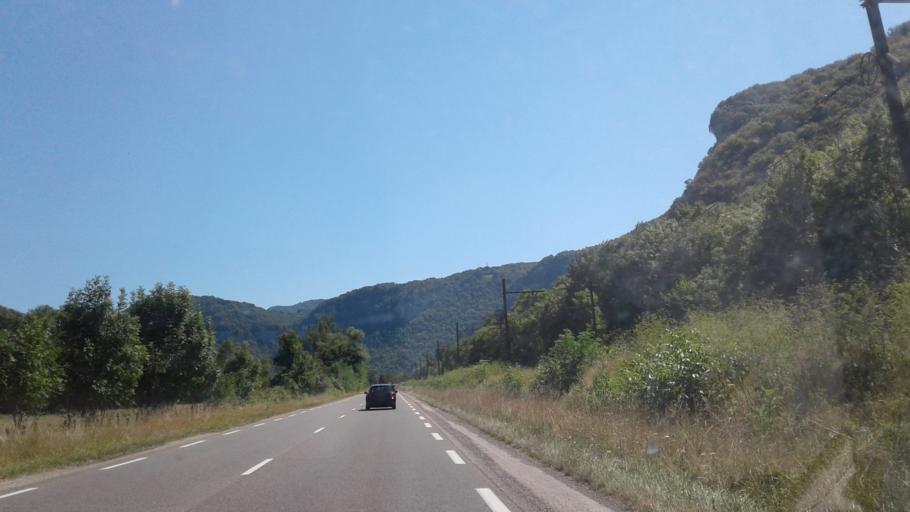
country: FR
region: Rhone-Alpes
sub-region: Departement de l'Ain
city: Vaux-en-Bugey
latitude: 45.9322
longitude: 5.3832
